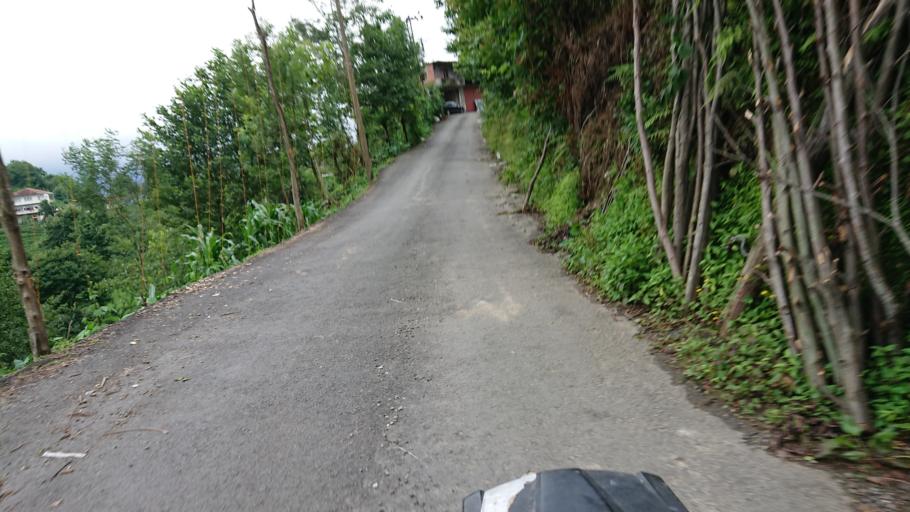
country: TR
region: Rize
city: Rize
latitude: 40.9716
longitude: 40.5168
